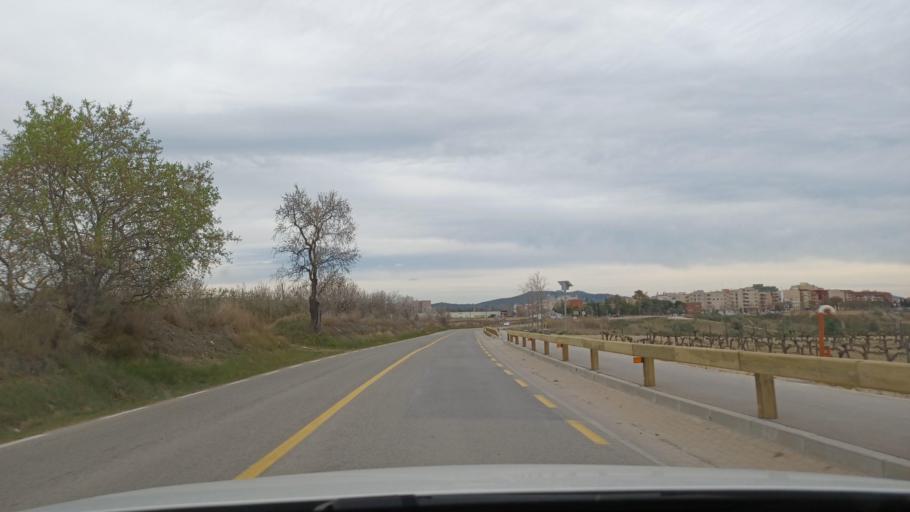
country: ES
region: Catalonia
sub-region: Provincia de Barcelona
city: Vilafranca del Penedes
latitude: 41.3600
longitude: 1.6975
